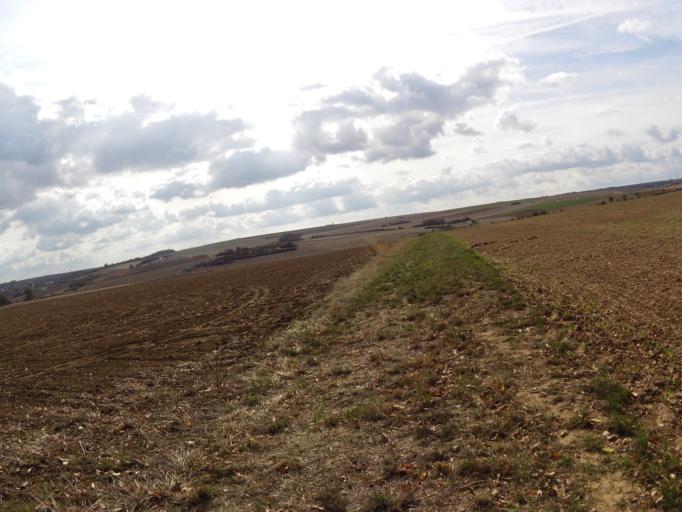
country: DE
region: Bavaria
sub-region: Regierungsbezirk Unterfranken
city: Reichenberg
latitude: 49.7358
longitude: 9.9410
